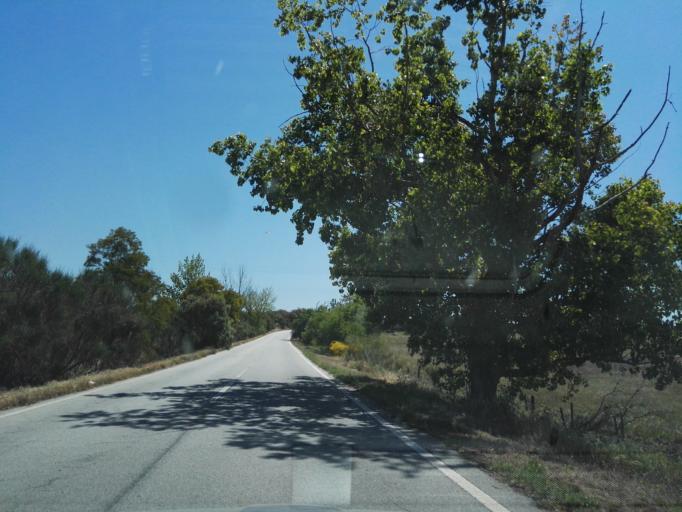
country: PT
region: Portalegre
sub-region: Arronches
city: Arronches
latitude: 39.0069
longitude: -7.2334
